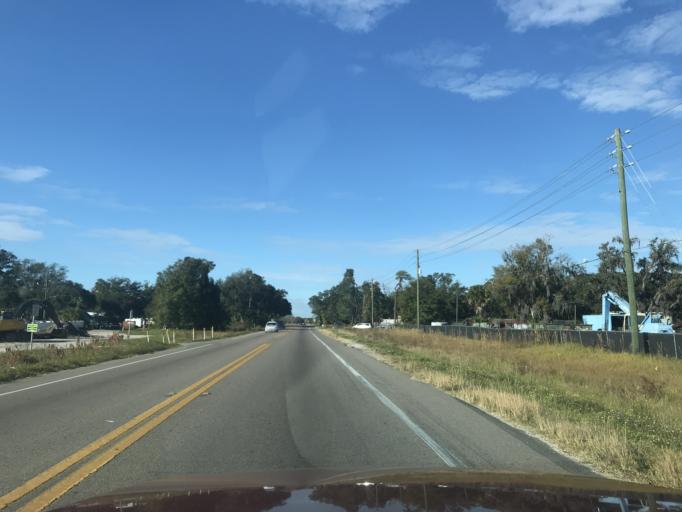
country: US
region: Florida
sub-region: Osceola County
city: Campbell
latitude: 28.2560
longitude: -81.4676
